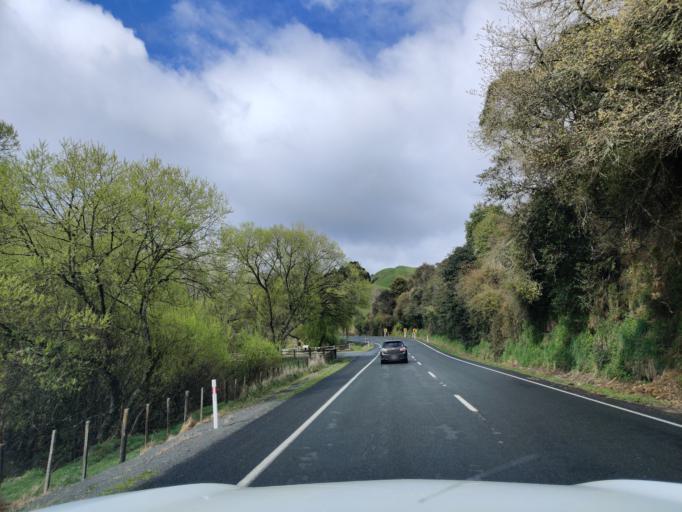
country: NZ
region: Waikato
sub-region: Otorohanga District
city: Otorohanga
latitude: -38.6046
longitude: 175.2159
